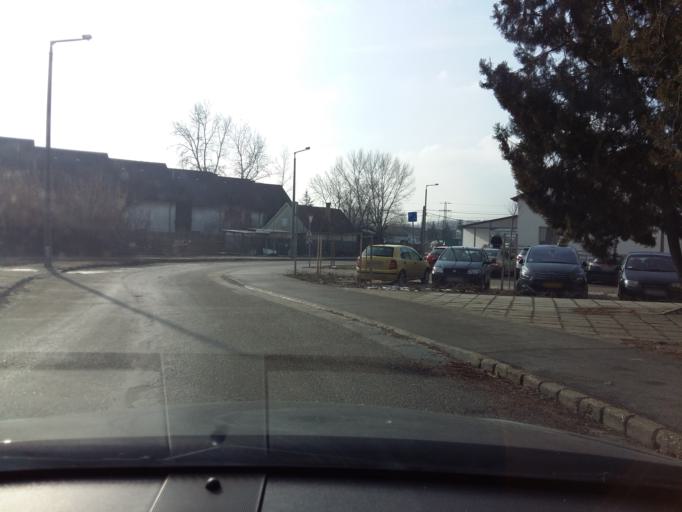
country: HU
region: Pest
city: Szigetszentmiklos
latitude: 47.3393
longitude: 19.0307
